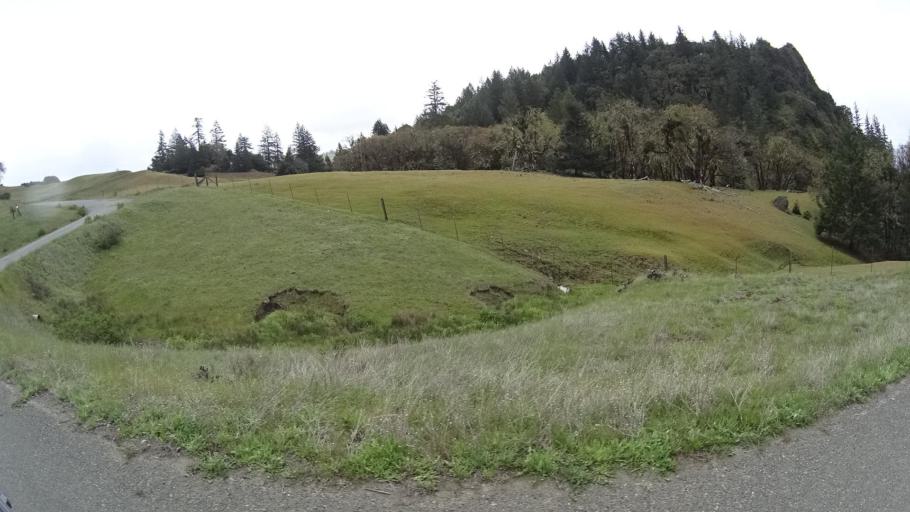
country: US
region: California
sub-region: Humboldt County
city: Redway
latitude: 40.1572
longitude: -123.5515
